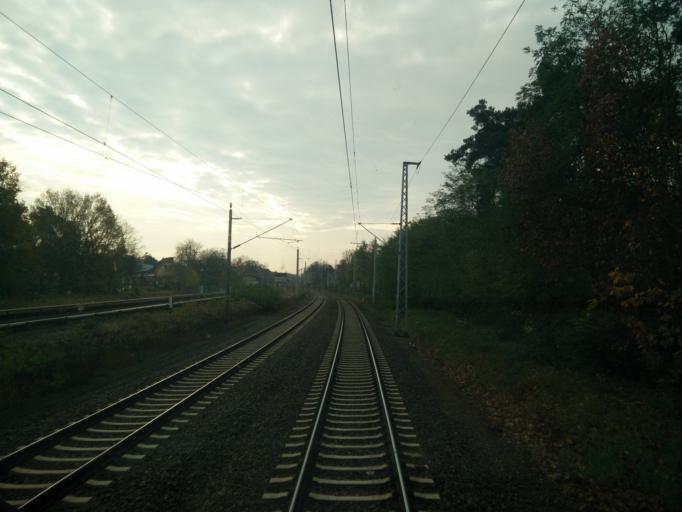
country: DE
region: Brandenburg
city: Zeuthen
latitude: 52.3523
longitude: 13.6246
